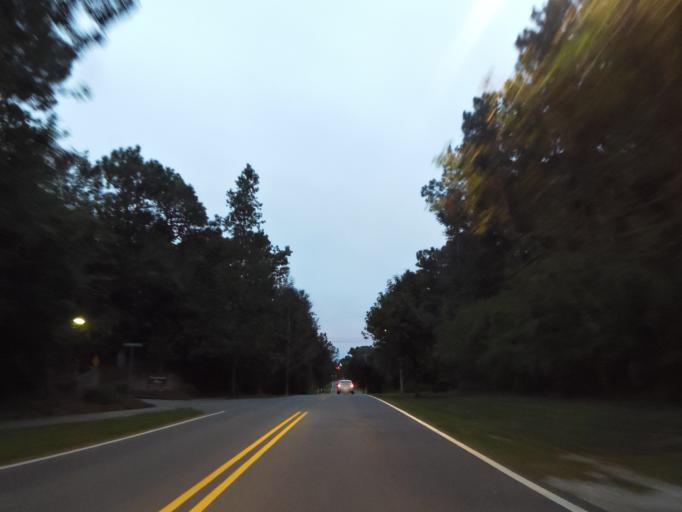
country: US
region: Alabama
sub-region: Baldwin County
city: Fairhope
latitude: 30.5437
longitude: -87.8975
